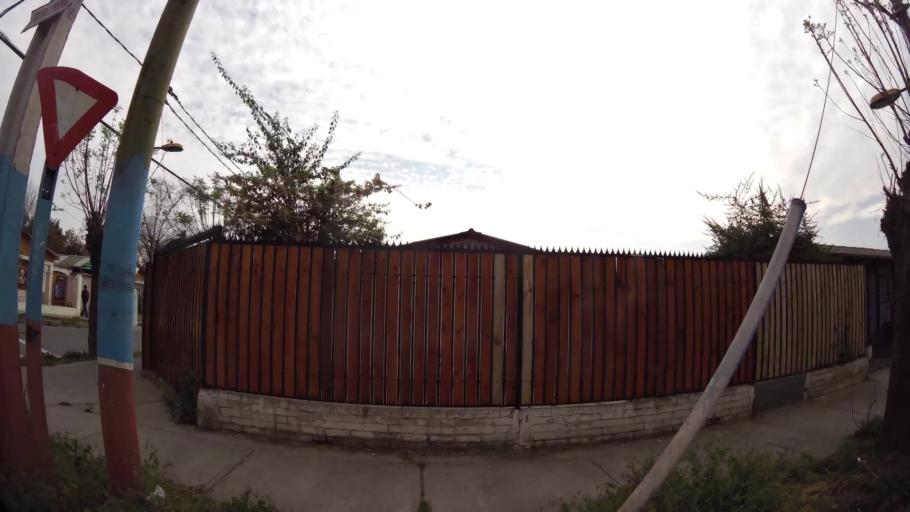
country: CL
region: Santiago Metropolitan
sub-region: Provincia de Santiago
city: Lo Prado
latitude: -33.5140
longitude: -70.7541
